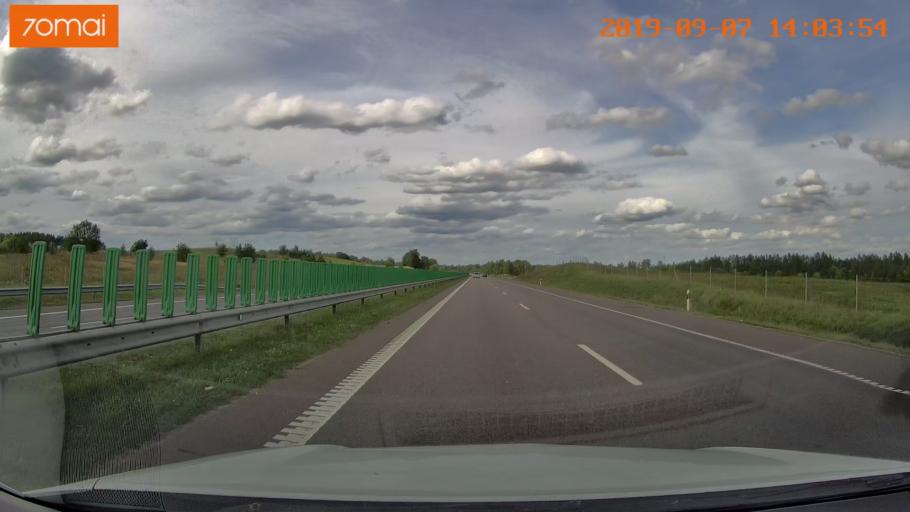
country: LT
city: Trakai
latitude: 54.7371
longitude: 24.9506
